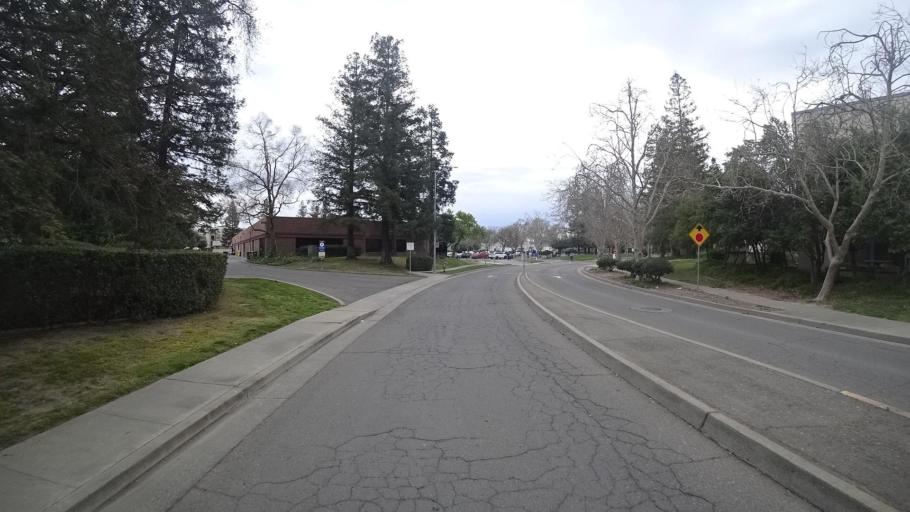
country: US
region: California
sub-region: Yolo County
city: Davis
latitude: 38.5386
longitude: -121.7315
